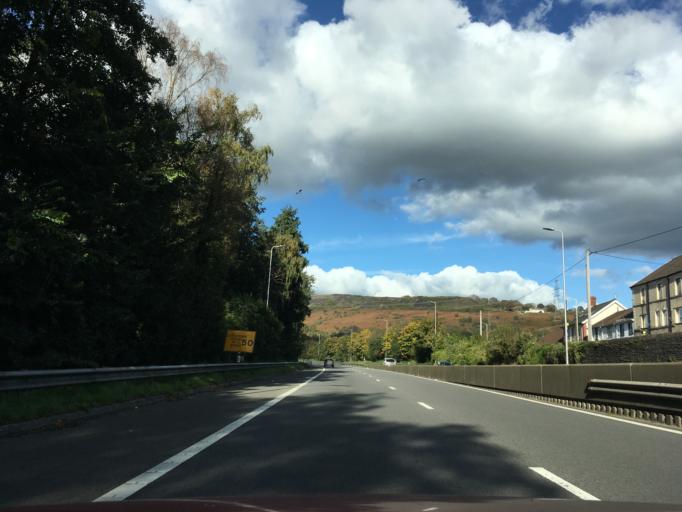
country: GB
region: Wales
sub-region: Rhondda Cynon Taf
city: Pontypridd
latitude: 51.6230
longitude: -3.3205
